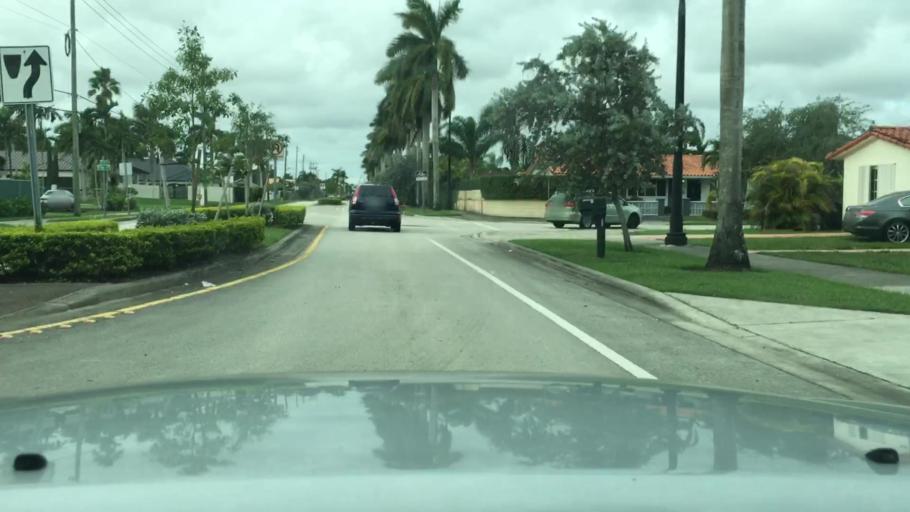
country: US
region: Florida
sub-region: Miami-Dade County
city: Sunset
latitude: 25.7126
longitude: -80.3507
